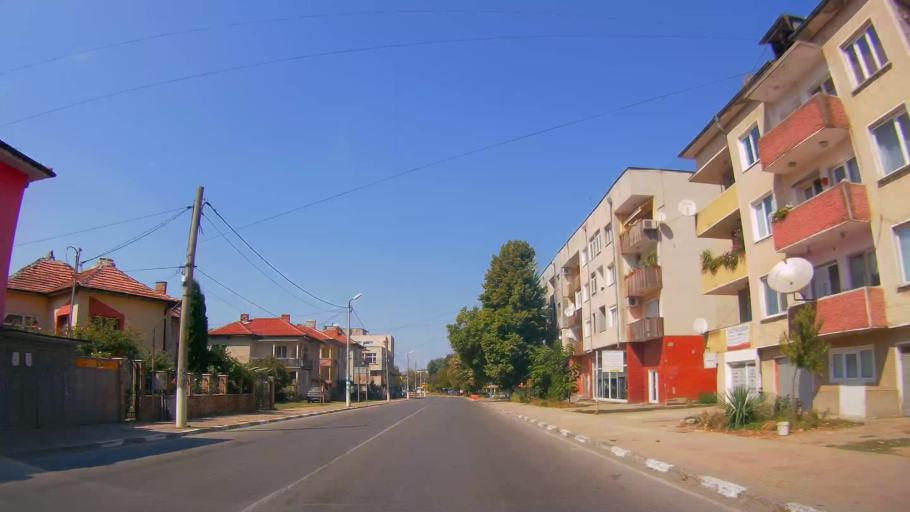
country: BG
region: Razgrad
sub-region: Obshtina Tsar Kaloyan
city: Tsar Kaloyan
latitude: 43.6075
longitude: 26.2385
